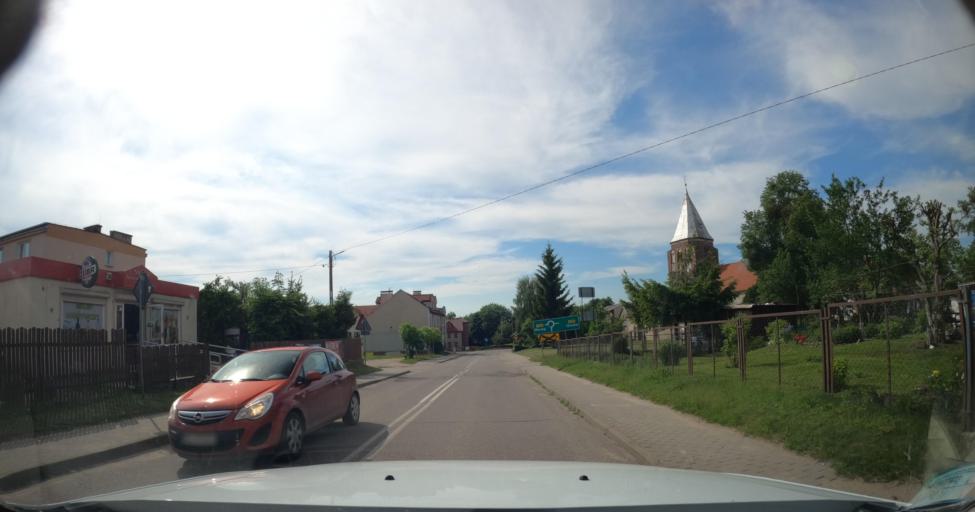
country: PL
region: Warmian-Masurian Voivodeship
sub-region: Powiat ostrodzki
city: Milakowo
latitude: 54.0098
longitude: 20.0736
